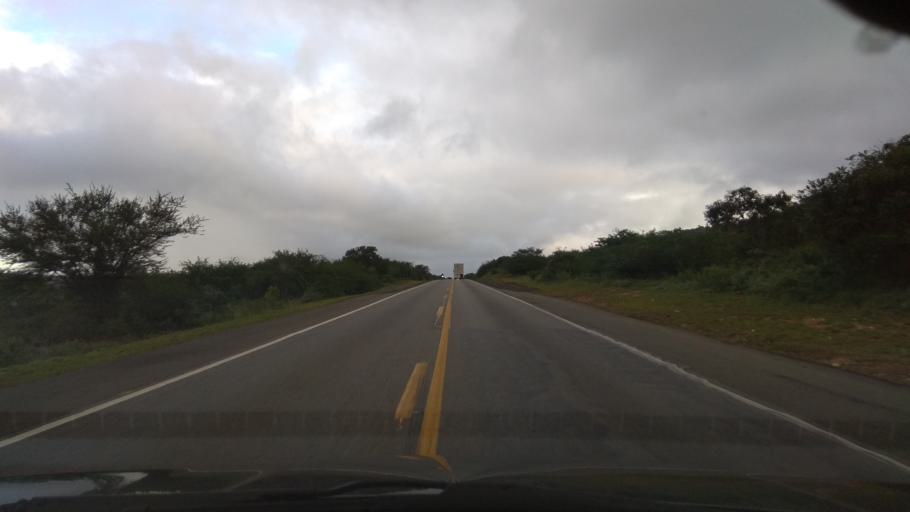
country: BR
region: Bahia
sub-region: Jaguaquara
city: Jaguaquara
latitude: -13.3446
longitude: -40.0165
